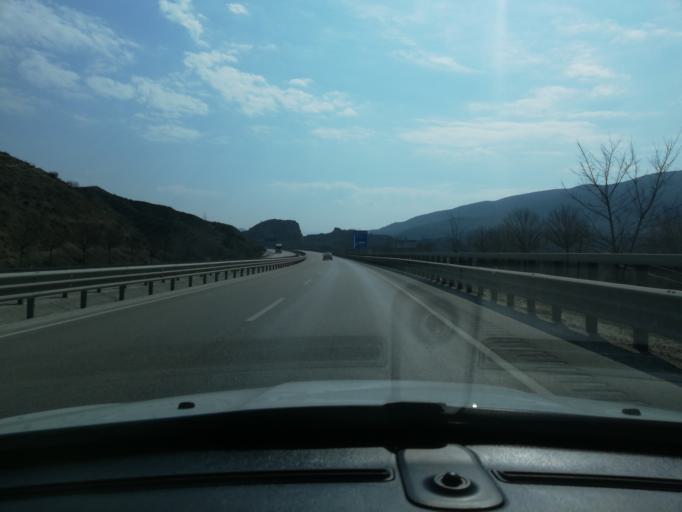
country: TR
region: Cankiri
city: Ilgaz
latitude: 40.9075
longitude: 33.6112
